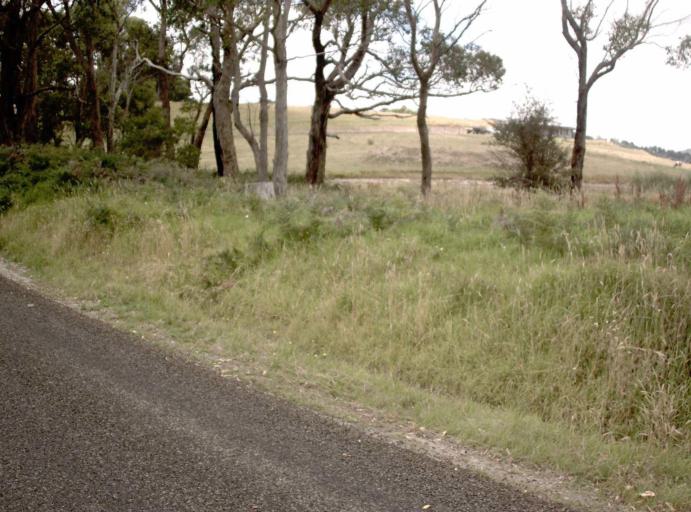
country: AU
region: Victoria
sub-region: Cardinia
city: Bunyip
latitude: -38.3355
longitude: 145.6983
